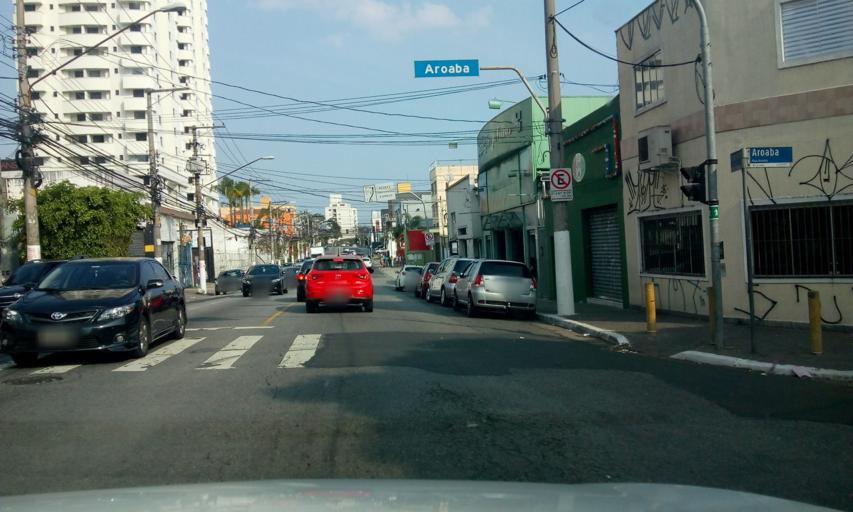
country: BR
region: Sao Paulo
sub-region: Osasco
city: Osasco
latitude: -23.5329
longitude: -46.7291
